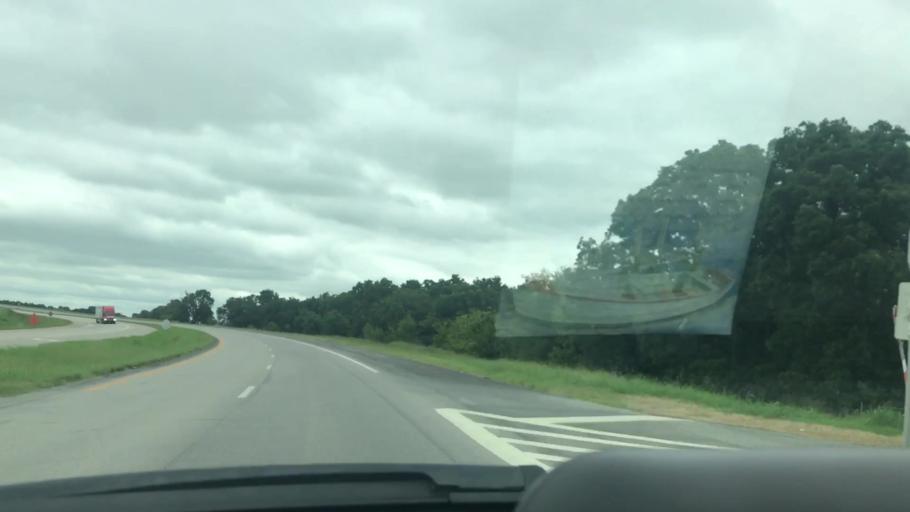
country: US
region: Oklahoma
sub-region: Mayes County
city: Pryor
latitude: 36.3655
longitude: -95.2923
